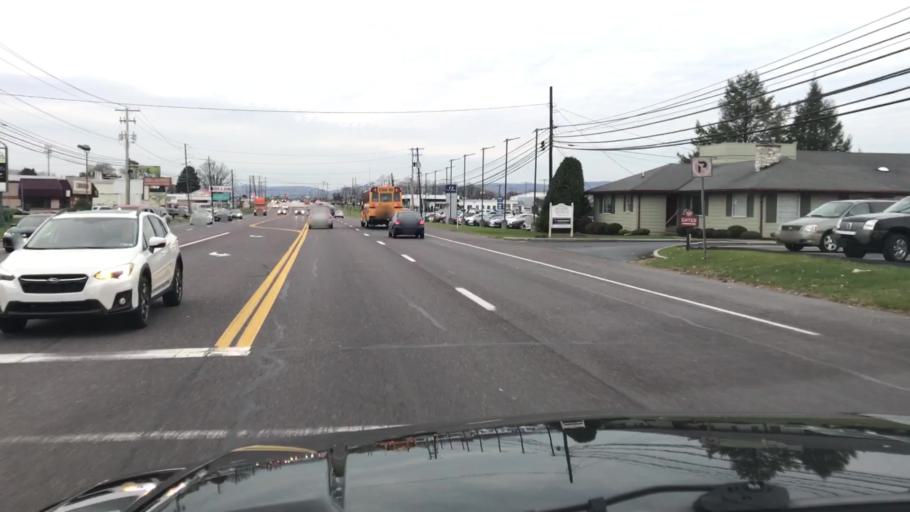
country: US
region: Pennsylvania
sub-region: Cumberland County
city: Mechanicsburg
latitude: 40.2438
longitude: -76.9935
